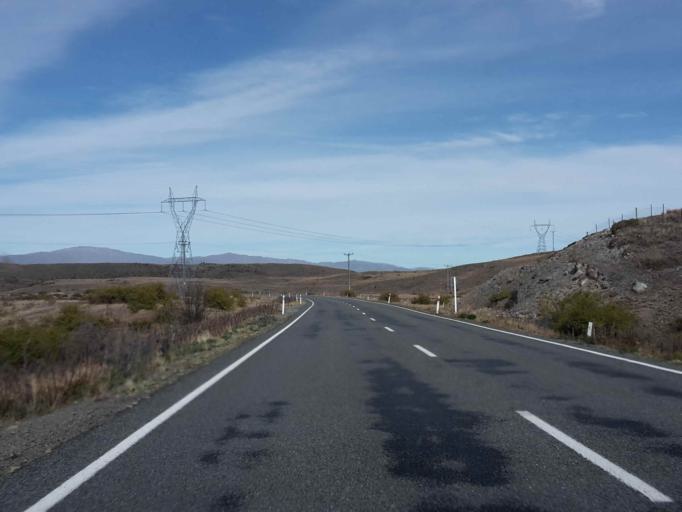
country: NZ
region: Canterbury
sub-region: Timaru District
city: Pleasant Point
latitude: -44.1722
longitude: 170.2159
